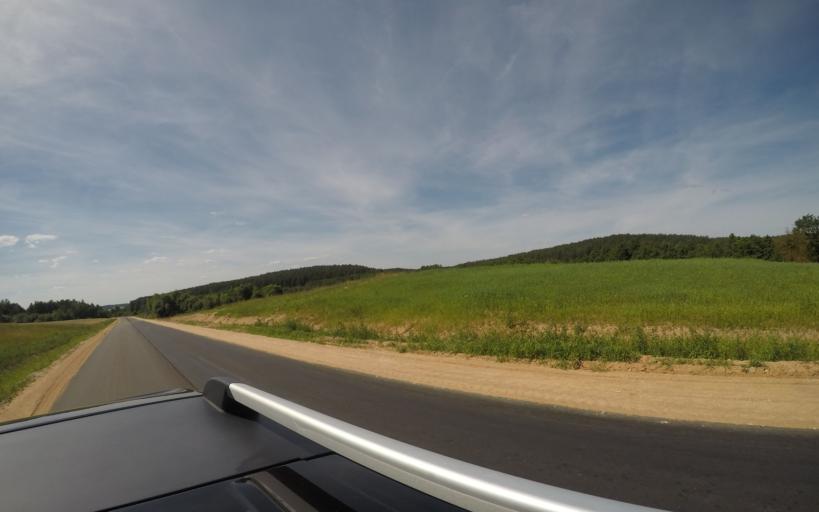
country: BY
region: Grodnenskaya
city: Hal'shany
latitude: 54.2591
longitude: 25.9750
